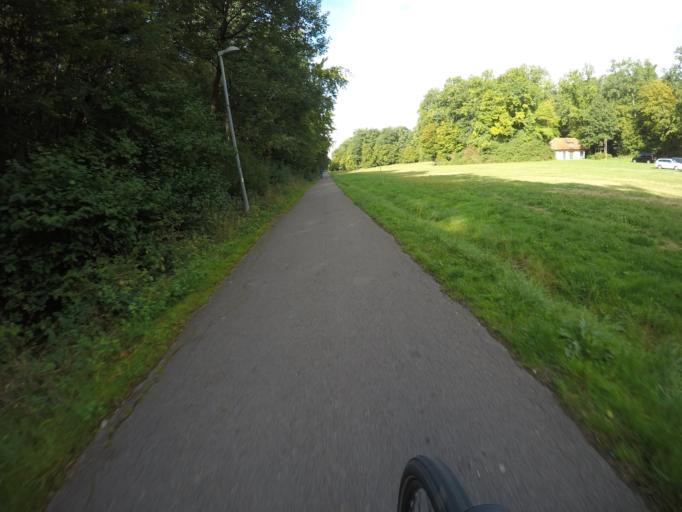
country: DE
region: Baden-Wuerttemberg
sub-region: Regierungsbezirk Stuttgart
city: Sindelfingen
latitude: 48.7252
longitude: 8.9979
